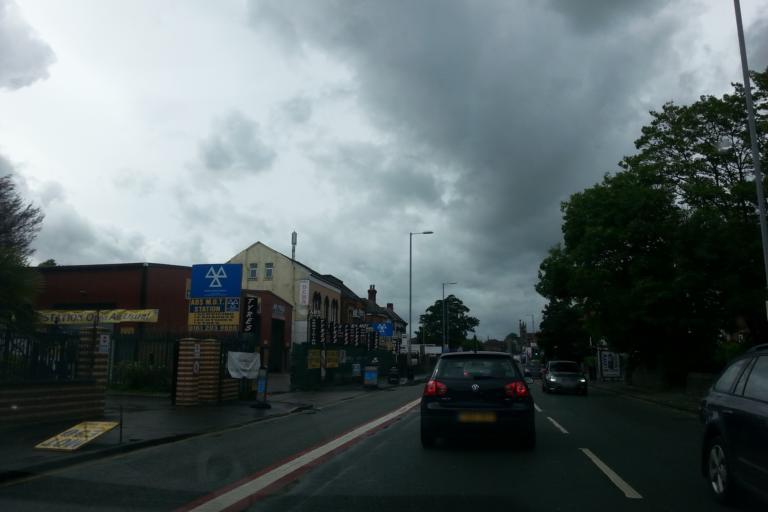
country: GB
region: England
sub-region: Manchester
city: Cheetham Hill
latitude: 53.5058
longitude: -2.2374
